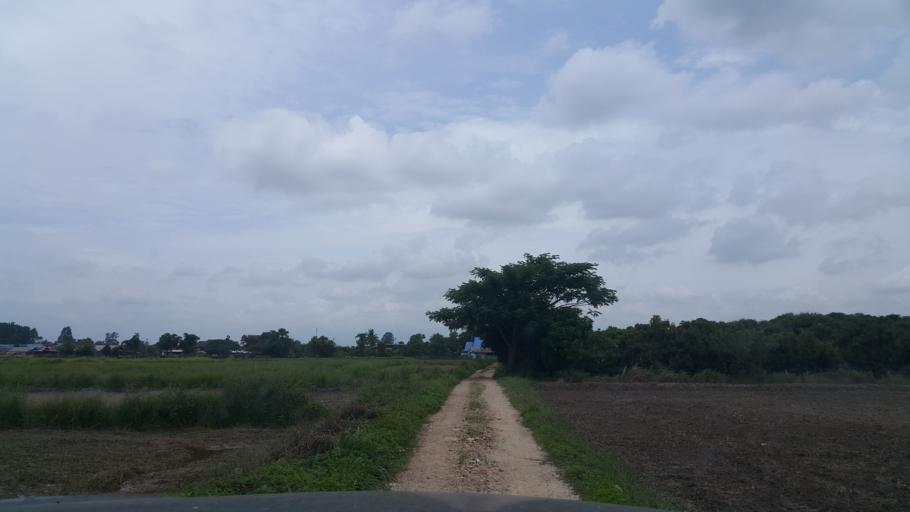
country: TH
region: Lamphun
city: Ban Thi
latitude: 18.6417
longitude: 99.1457
